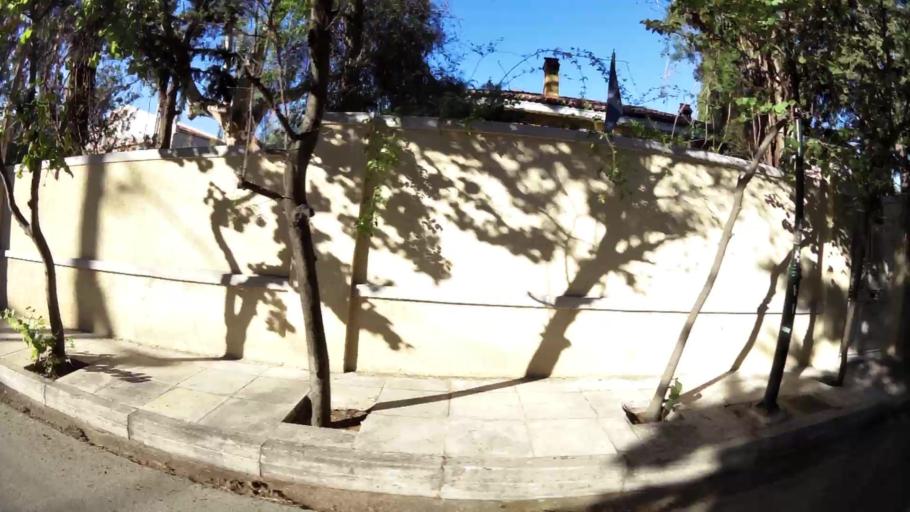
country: GR
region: Attica
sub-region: Nomarchia Athinas
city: Kifisia
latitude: 38.0781
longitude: 23.8020
